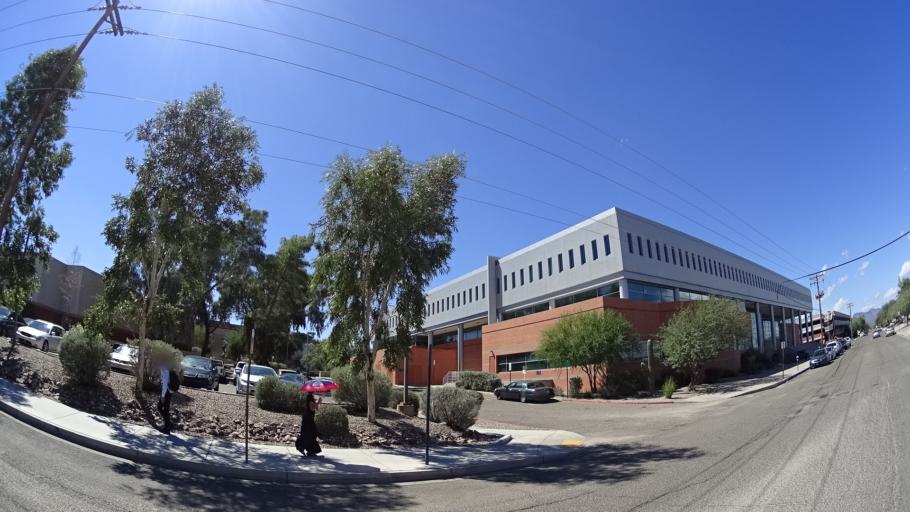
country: US
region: Arizona
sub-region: Pima County
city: Tucson
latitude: 32.2373
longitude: -110.9536
